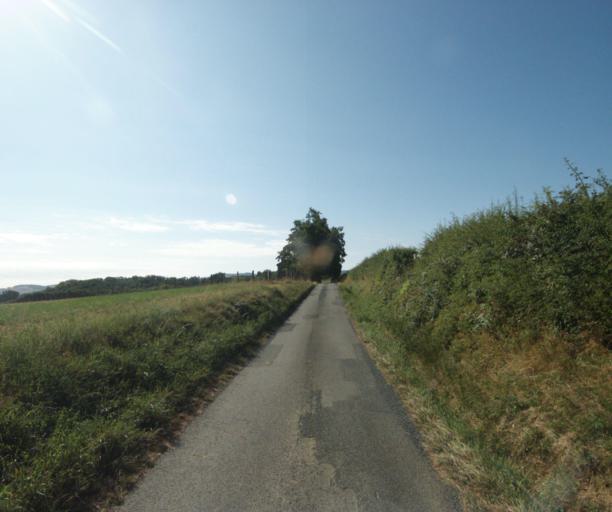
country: FR
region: Rhone-Alpes
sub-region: Departement du Rhone
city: Savigny
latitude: 45.8129
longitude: 4.5795
